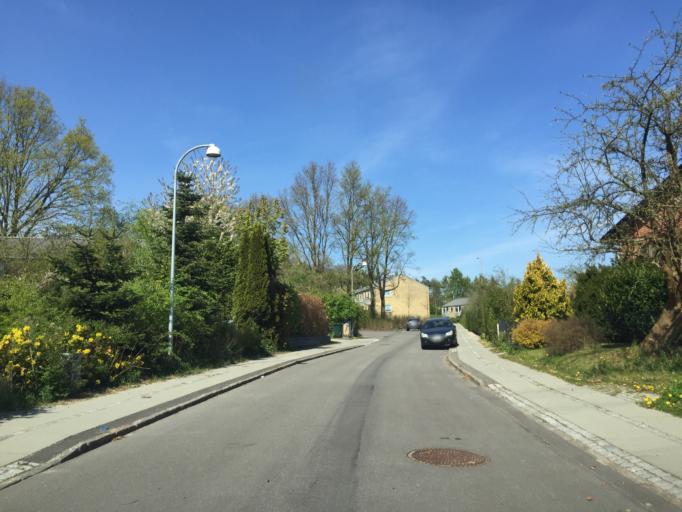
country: DK
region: Capital Region
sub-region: Gladsaxe Municipality
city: Buddinge
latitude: 55.7297
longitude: 12.5019
